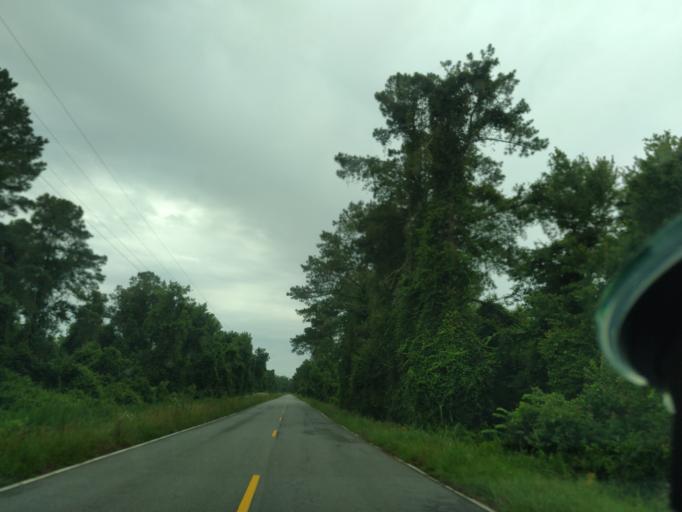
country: US
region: North Carolina
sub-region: Washington County
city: Plymouth
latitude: 35.7945
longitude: -76.5179
